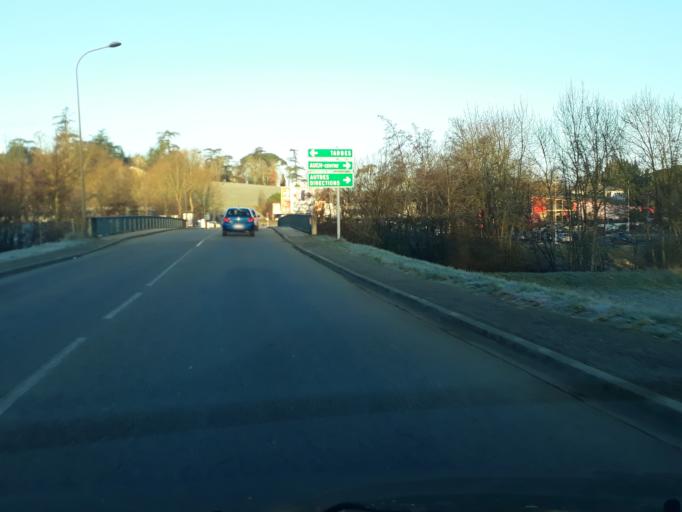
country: FR
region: Midi-Pyrenees
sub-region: Departement du Gers
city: Auch
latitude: 43.6304
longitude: 0.5836
